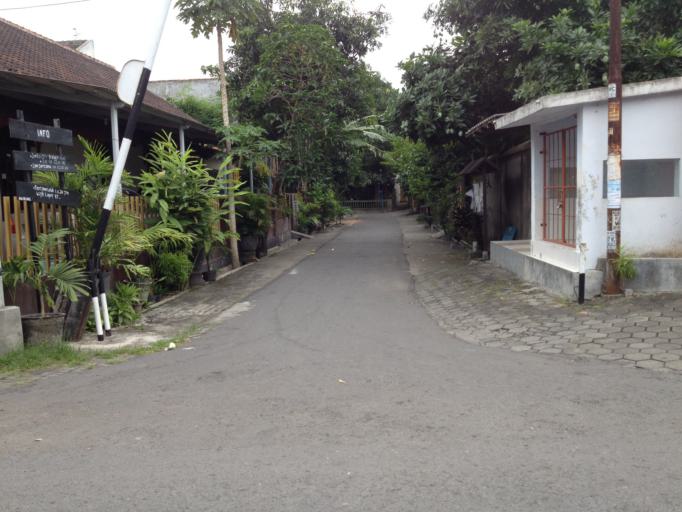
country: ID
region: Daerah Istimewa Yogyakarta
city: Yogyakarta
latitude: -7.8248
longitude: 110.3771
